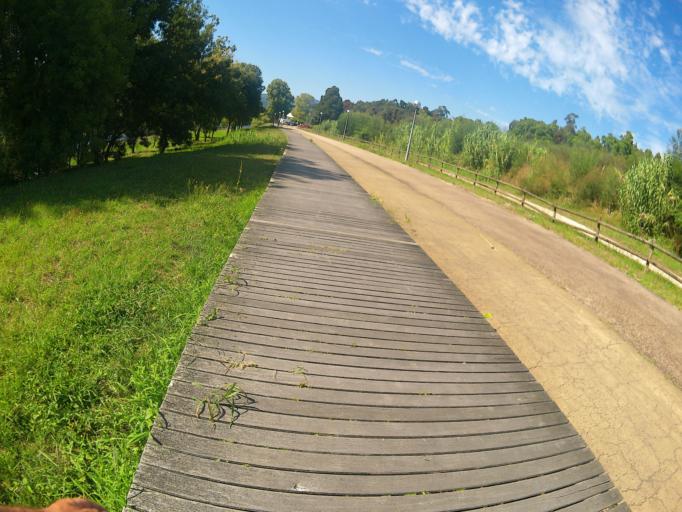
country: PT
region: Viana do Castelo
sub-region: Valenca
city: Valenca
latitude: 42.0219
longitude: -8.6563
